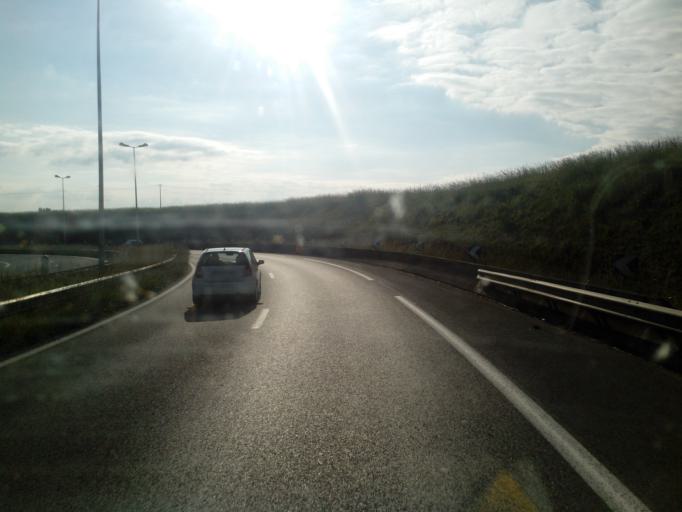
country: FR
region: Lower Normandy
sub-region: Departement du Calvados
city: Authie
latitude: 49.1920
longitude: -0.4216
